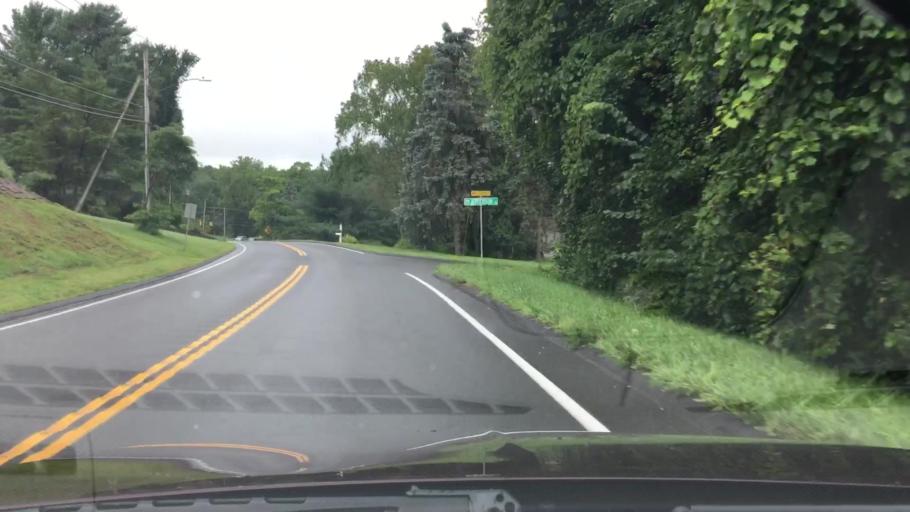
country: US
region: Connecticut
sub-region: Hartford County
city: Tariffville
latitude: 41.9276
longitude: -72.7630
